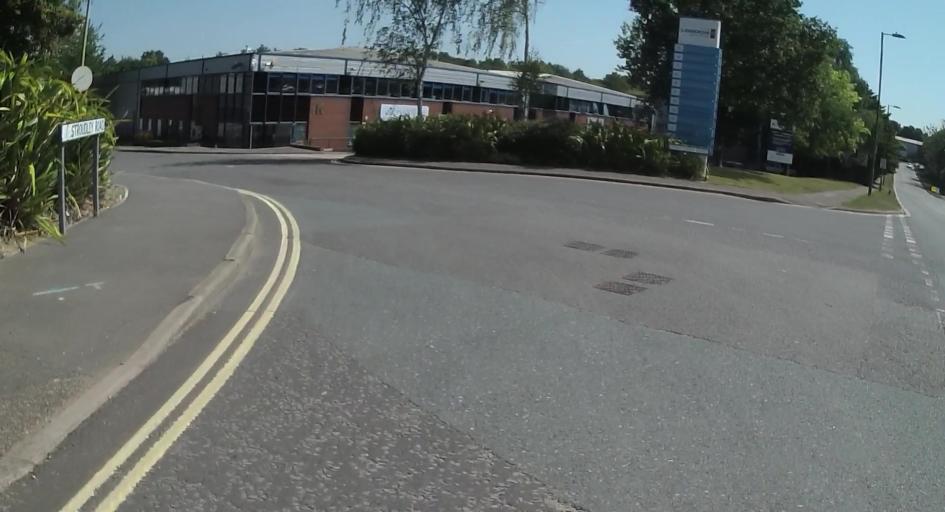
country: GB
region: England
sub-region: Hampshire
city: Basingstoke
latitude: 51.2785
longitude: -1.0658
